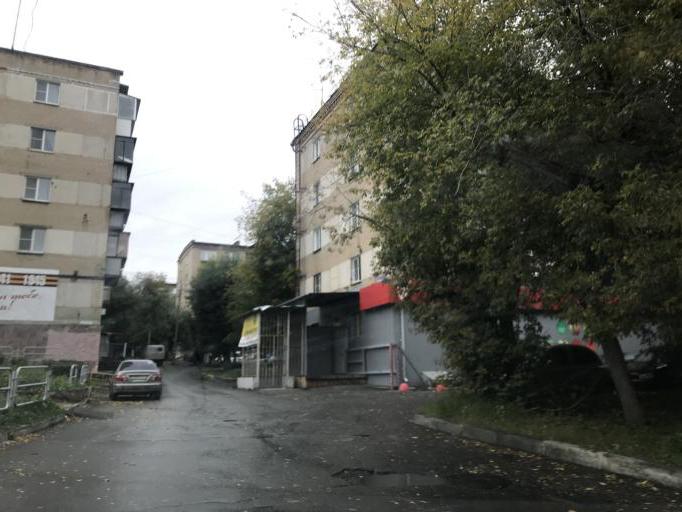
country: RU
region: Chelyabinsk
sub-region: Gorod Chelyabinsk
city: Chelyabinsk
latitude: 55.1844
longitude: 61.3917
